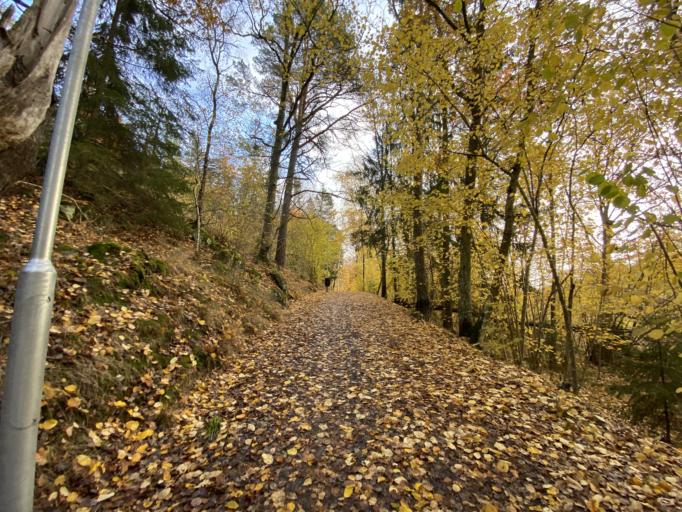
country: SE
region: Stockholm
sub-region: Salems Kommun
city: Ronninge
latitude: 59.1874
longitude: 17.7304
